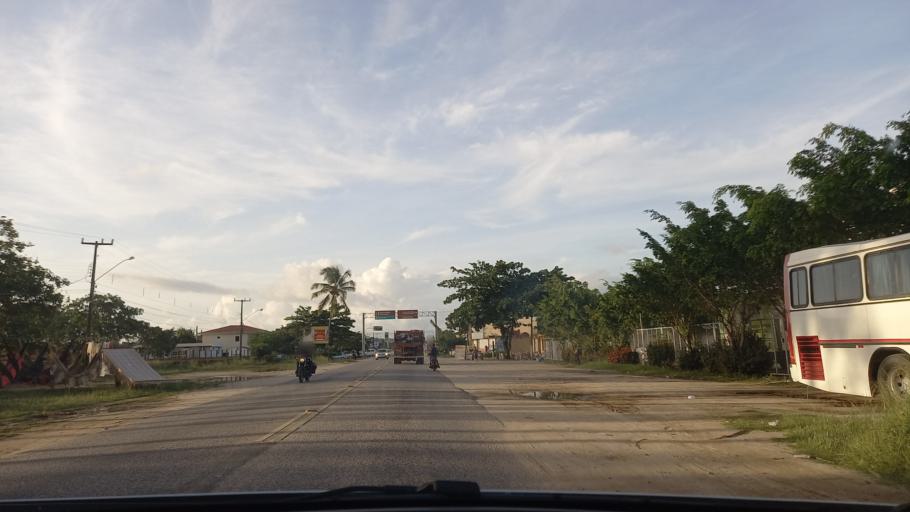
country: BR
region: Pernambuco
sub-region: Sao Jose Da Coroa Grande
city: Sao Jose da Coroa Grande
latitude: -8.8967
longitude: -35.1506
